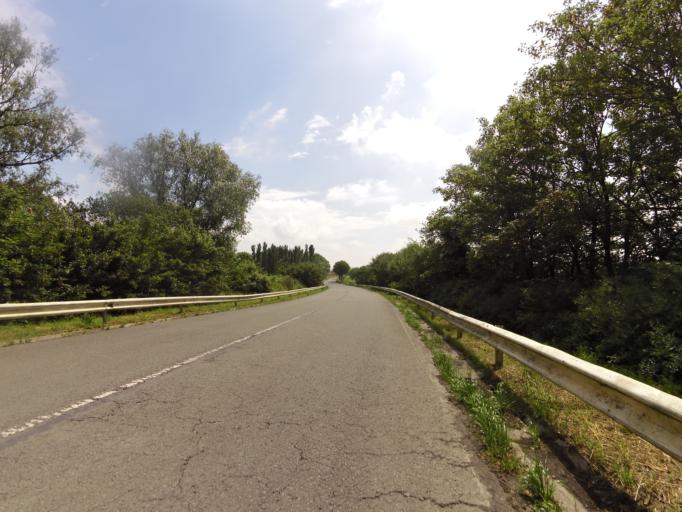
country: BE
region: Flanders
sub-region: Provincie West-Vlaanderen
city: Middelkerke
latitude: 51.1318
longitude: 2.8141
